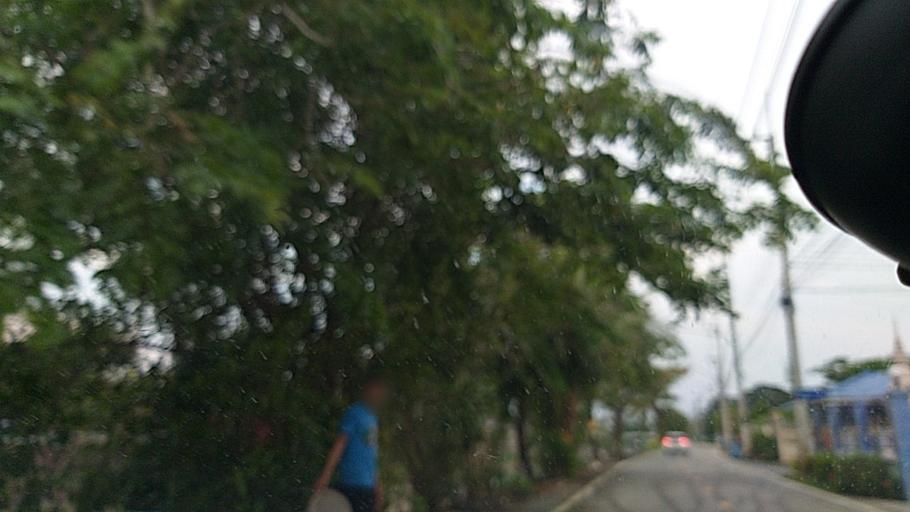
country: TH
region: Pathum Thani
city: Thanyaburi
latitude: 14.0629
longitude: 100.7098
